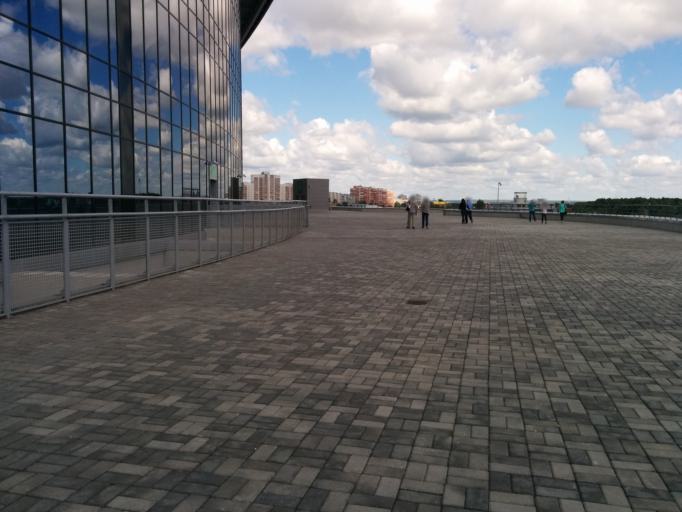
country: RU
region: Tatarstan
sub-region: Gorod Kazan'
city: Kazan
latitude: 55.8210
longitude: 49.1629
